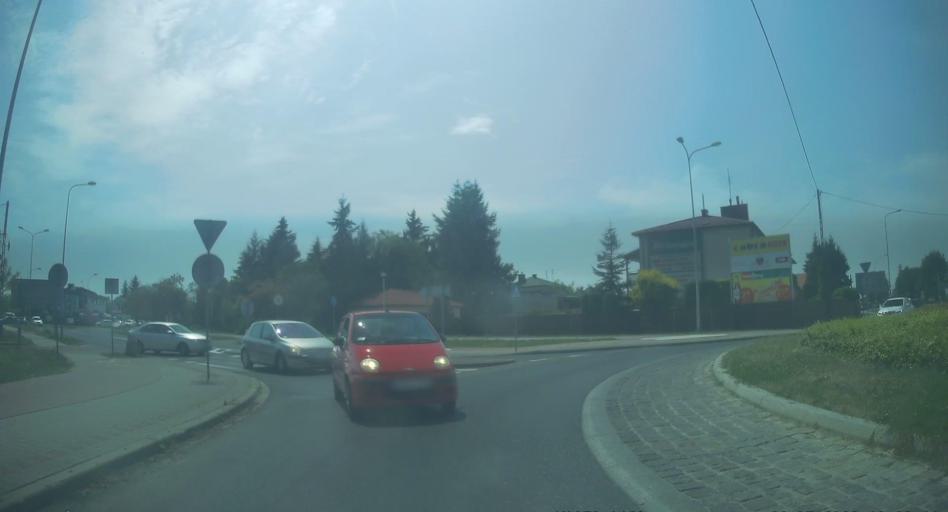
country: PL
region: Subcarpathian Voivodeship
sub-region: Powiat debicki
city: Debica
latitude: 50.0546
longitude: 21.4317
